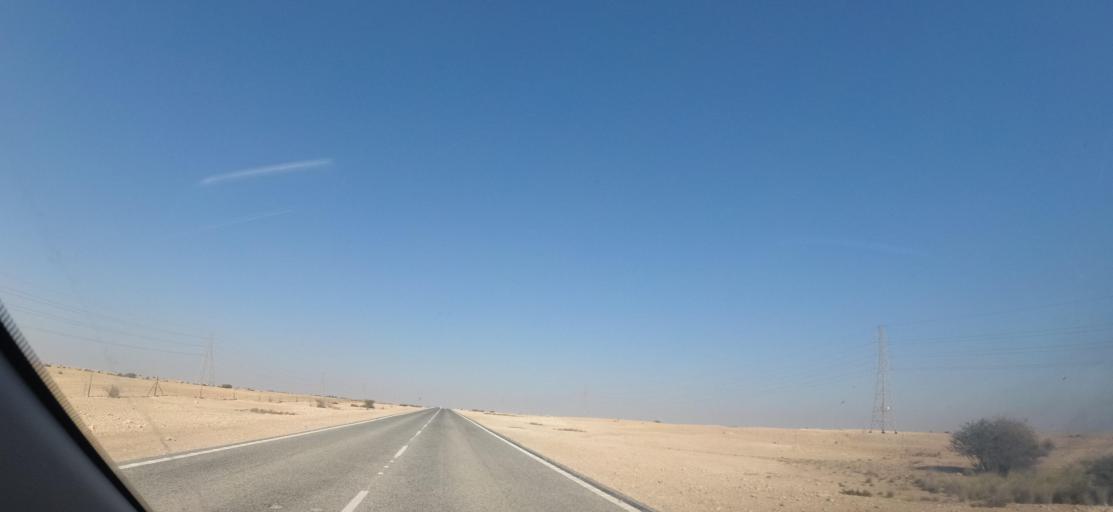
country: QA
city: Al Jumayliyah
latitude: 25.6485
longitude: 51.1100
